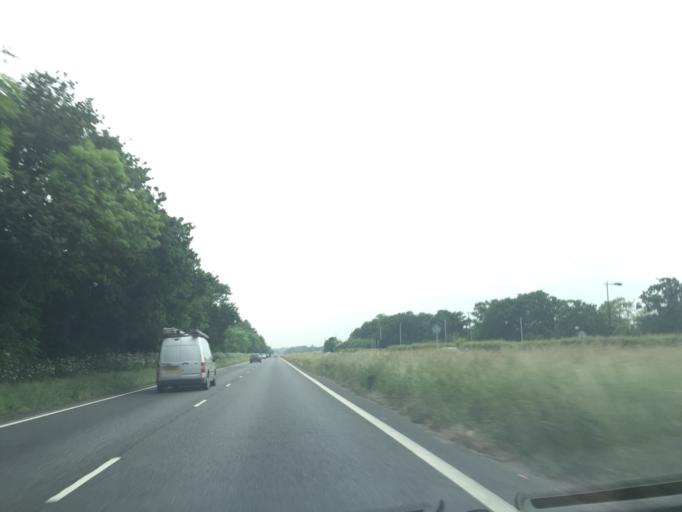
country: GB
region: England
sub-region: Poole
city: Poole
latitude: 50.7364
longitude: -1.9996
